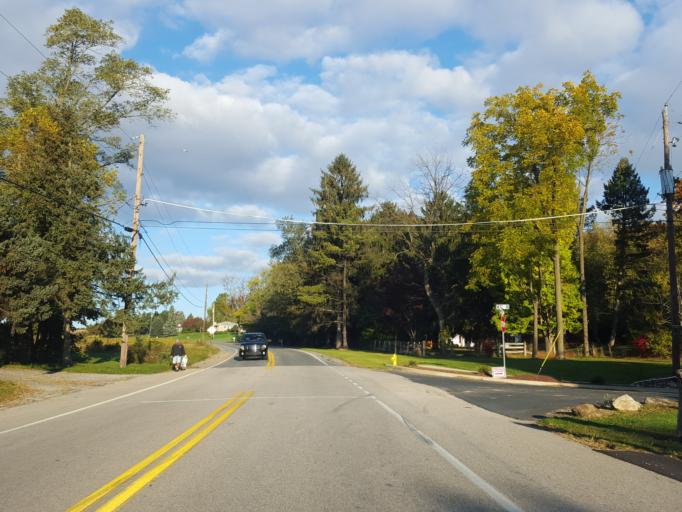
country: US
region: Pennsylvania
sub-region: York County
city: Stonybrook
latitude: 39.9517
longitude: -76.6333
